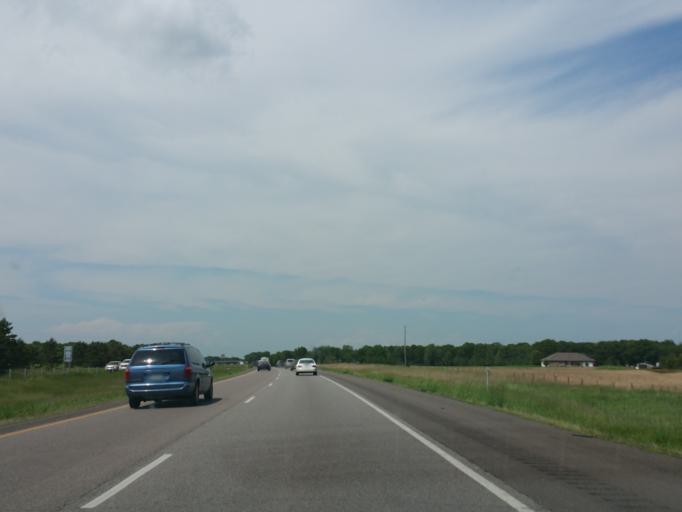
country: US
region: Minnesota
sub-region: Chisago County
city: Stacy
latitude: 45.4384
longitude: -92.9892
